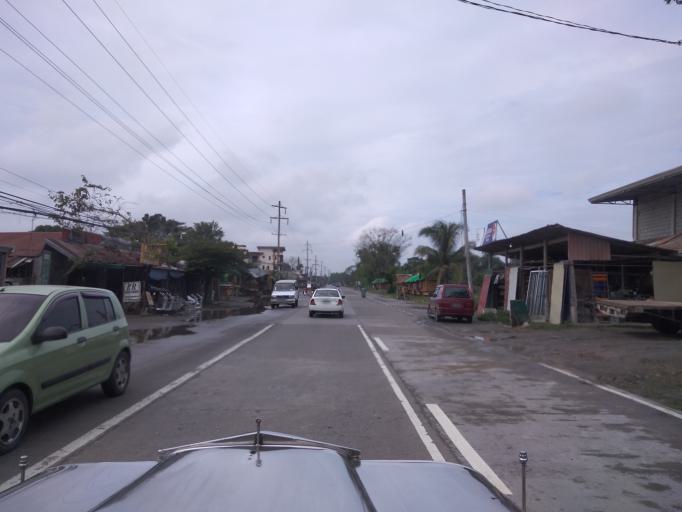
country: PH
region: Central Luzon
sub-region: Province of Pampanga
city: Santo Domingo
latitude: 15.0718
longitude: 120.7429
